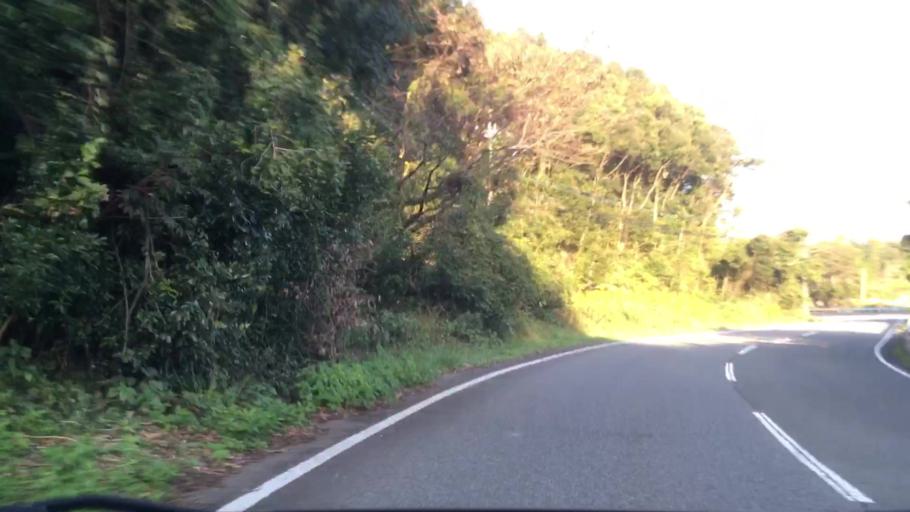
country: JP
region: Nagasaki
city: Sasebo
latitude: 32.9768
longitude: 129.7076
